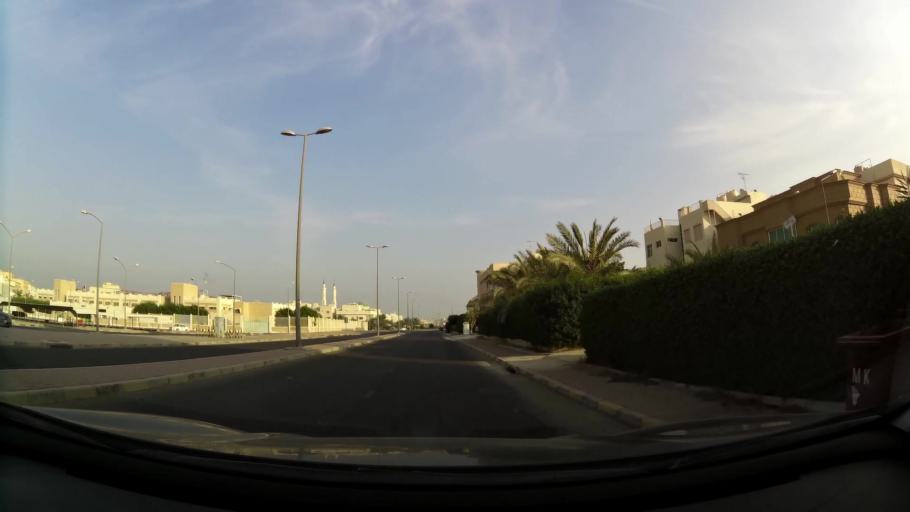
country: KW
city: Al Funaytis
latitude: 29.2308
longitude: 48.0803
